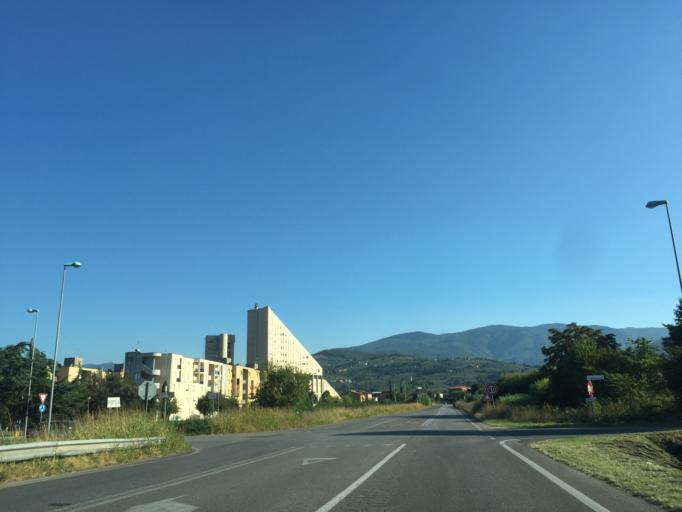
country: IT
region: Tuscany
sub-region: Provincia di Pistoia
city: Pistoia
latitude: 43.9426
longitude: 10.9347
